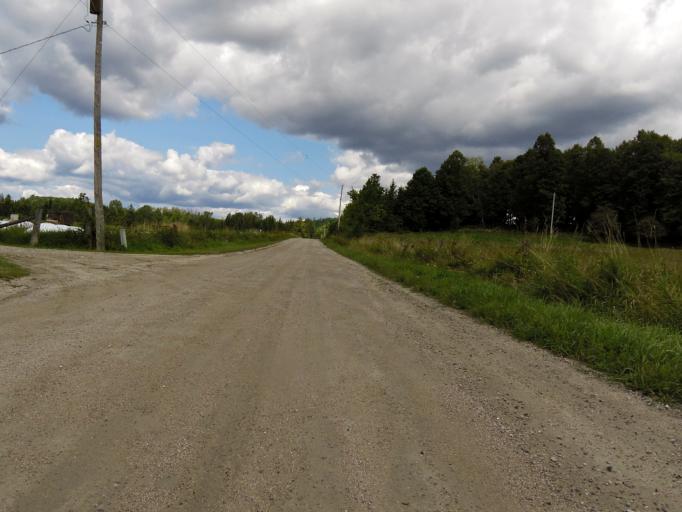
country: CA
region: Quebec
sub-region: Outaouais
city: Wakefield
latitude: 45.7904
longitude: -76.0274
